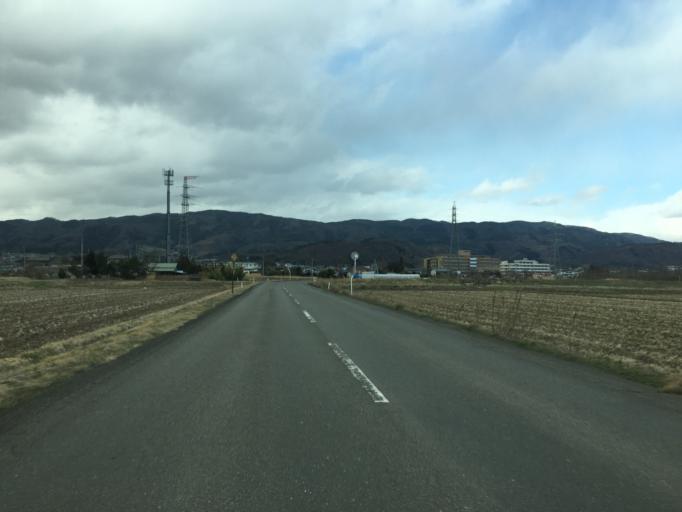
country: JP
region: Fukushima
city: Hobaramachi
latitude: 37.8658
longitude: 140.5379
